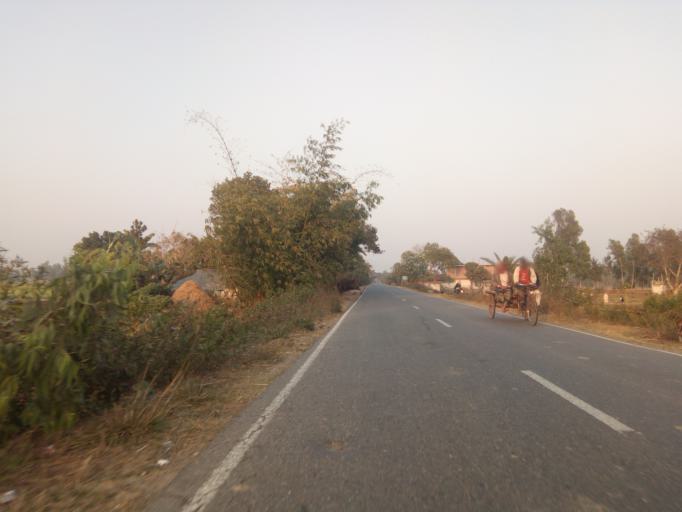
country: BD
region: Rajshahi
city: Bogra
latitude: 24.5869
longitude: 89.2309
